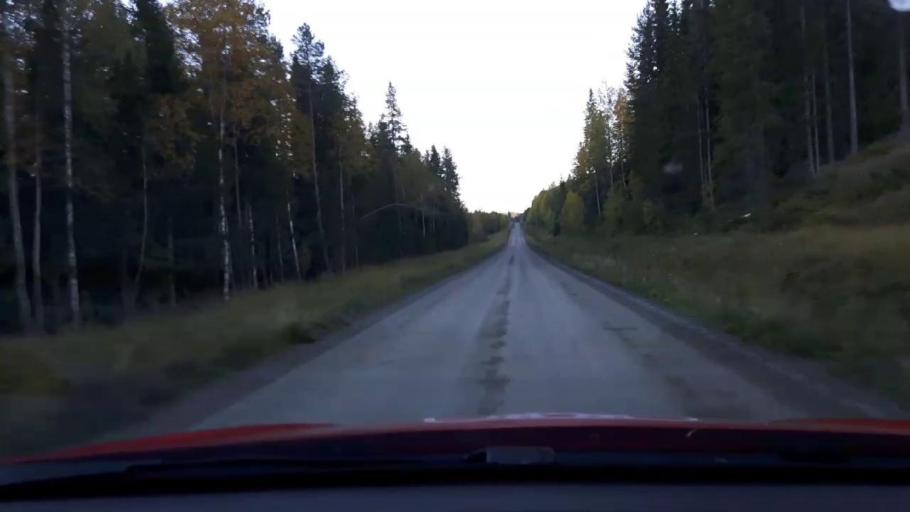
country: SE
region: Jaemtland
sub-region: OEstersunds Kommun
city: Brunflo
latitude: 62.9414
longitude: 14.9888
